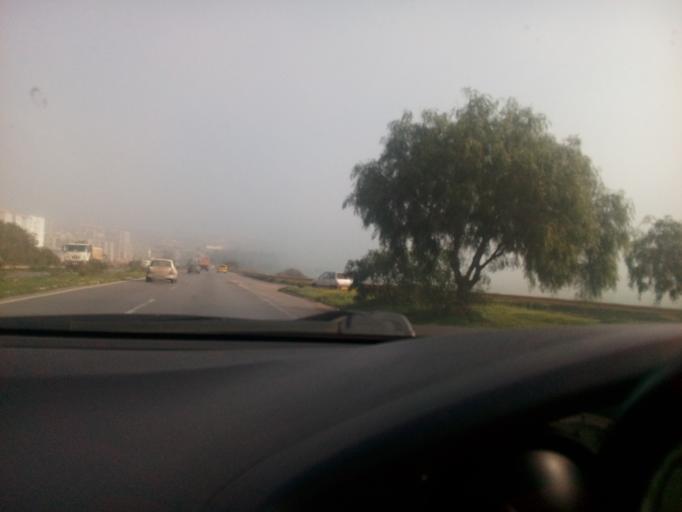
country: DZ
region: Oran
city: Es Senia
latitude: 35.6186
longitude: -0.7189
